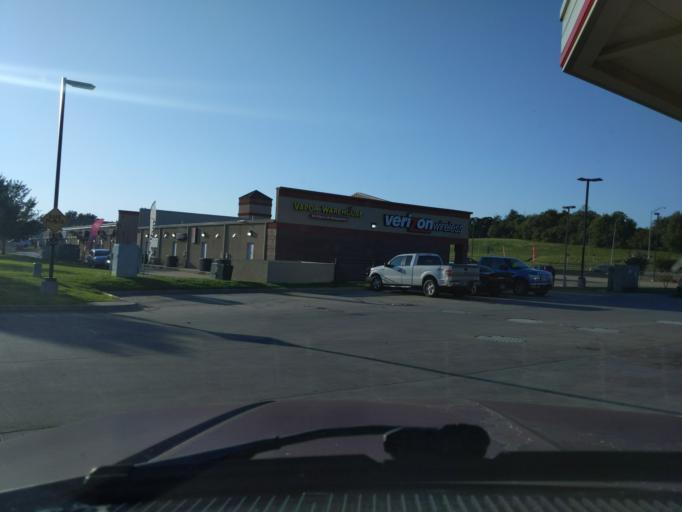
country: US
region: Oklahoma
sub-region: Tulsa County
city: Sand Springs
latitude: 36.1355
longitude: -96.1164
